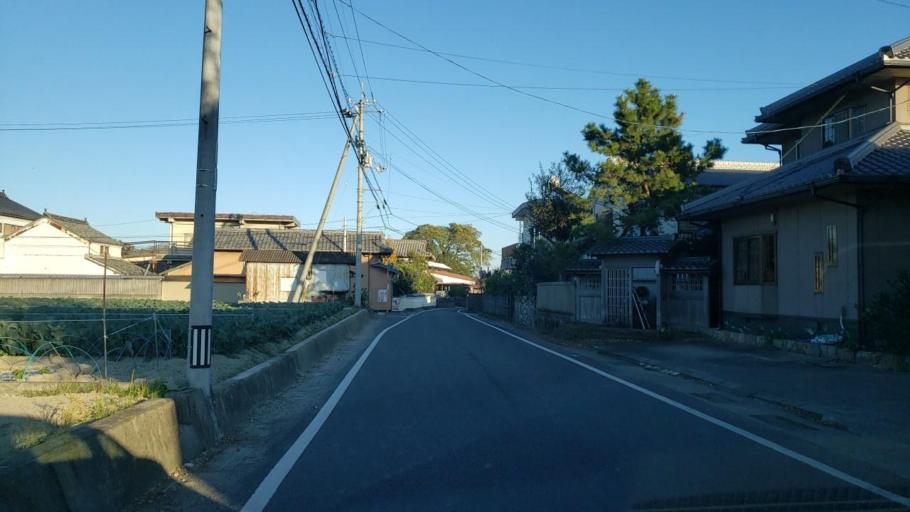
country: JP
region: Tokushima
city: Kamojimacho-jogejima
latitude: 34.0912
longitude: 134.2695
